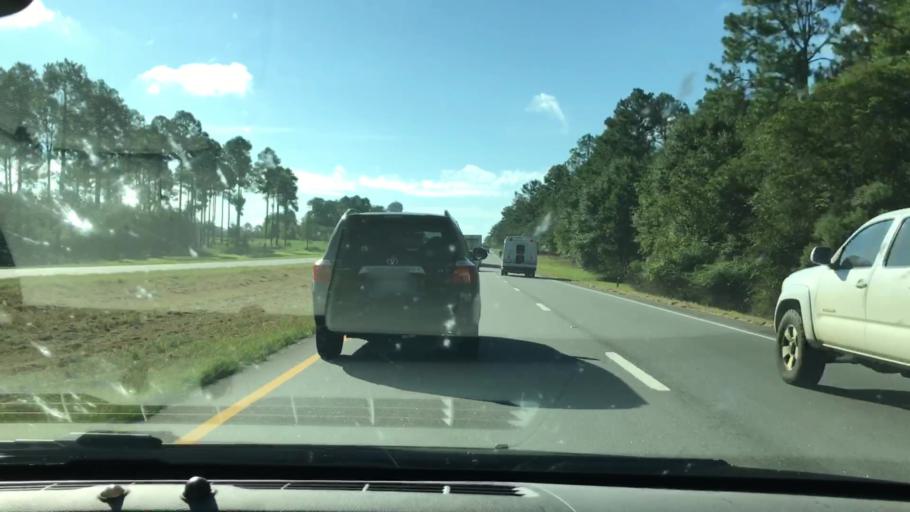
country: US
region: Georgia
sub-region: Dougherty County
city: Albany
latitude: 31.6448
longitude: -84.2573
